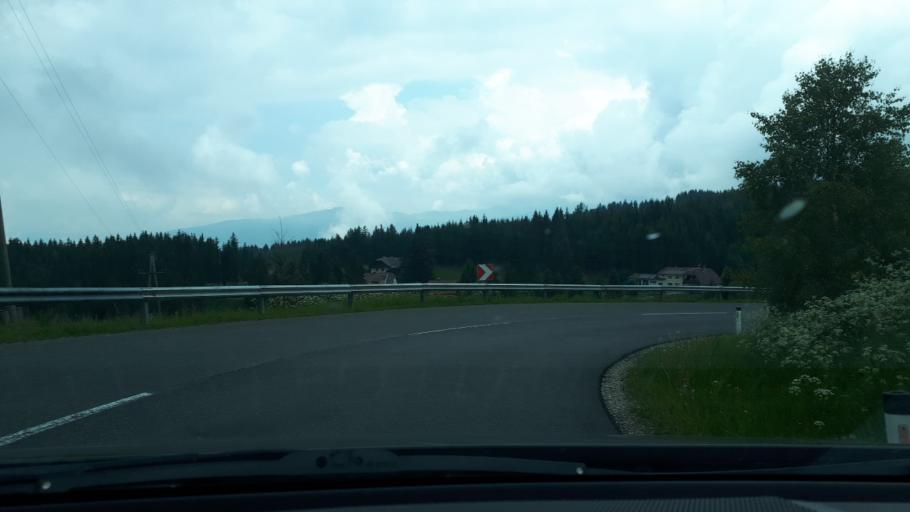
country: AT
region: Carinthia
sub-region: Politischer Bezirk Wolfsberg
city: Preitenegg
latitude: 46.9325
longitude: 14.9721
